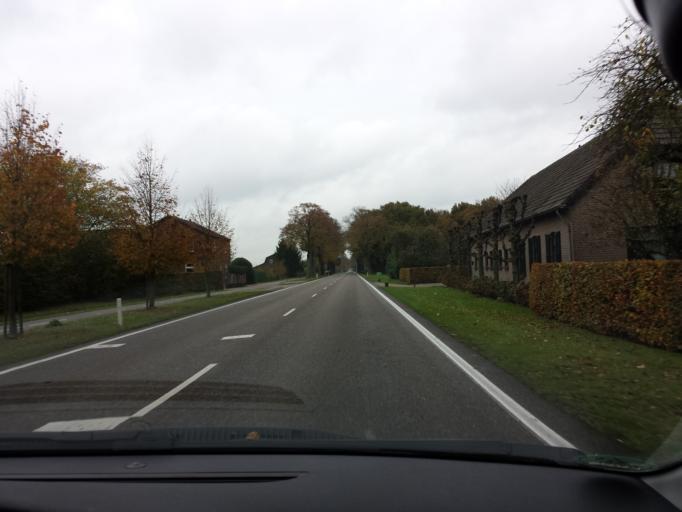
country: NL
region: Limburg
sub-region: Gemeente Venlo
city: Venlo
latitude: 51.4227
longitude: 6.1679
